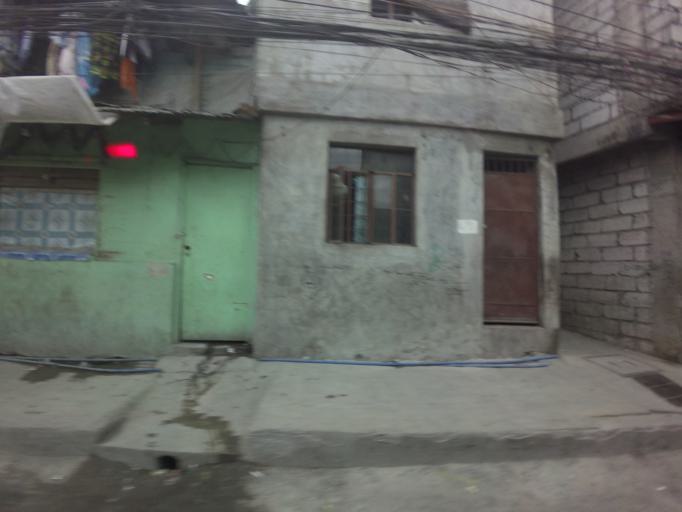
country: PH
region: Calabarzon
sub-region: Province of Rizal
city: Pateros
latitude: 14.5602
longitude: 121.0857
